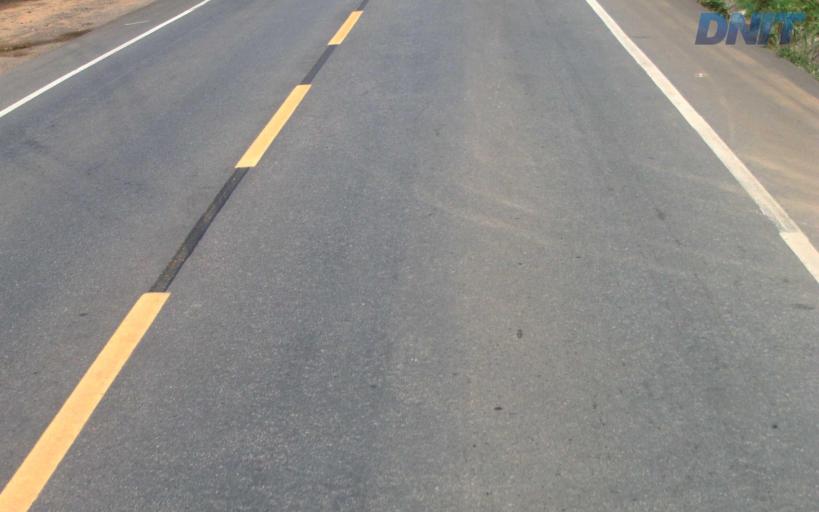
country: BR
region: Minas Gerais
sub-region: Ipaba
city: Ipaba
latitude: -19.2958
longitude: -42.3617
